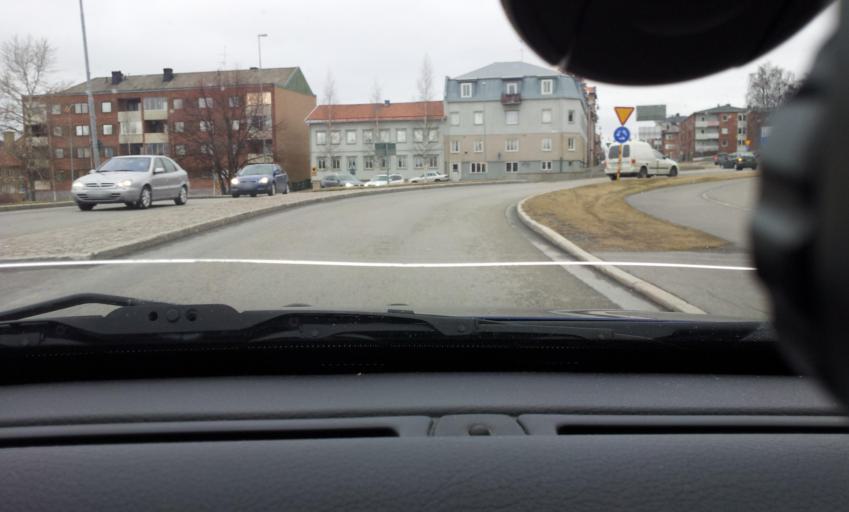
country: SE
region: Jaemtland
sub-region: OEstersunds Kommun
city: Ostersund
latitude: 63.1712
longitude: 14.6417
